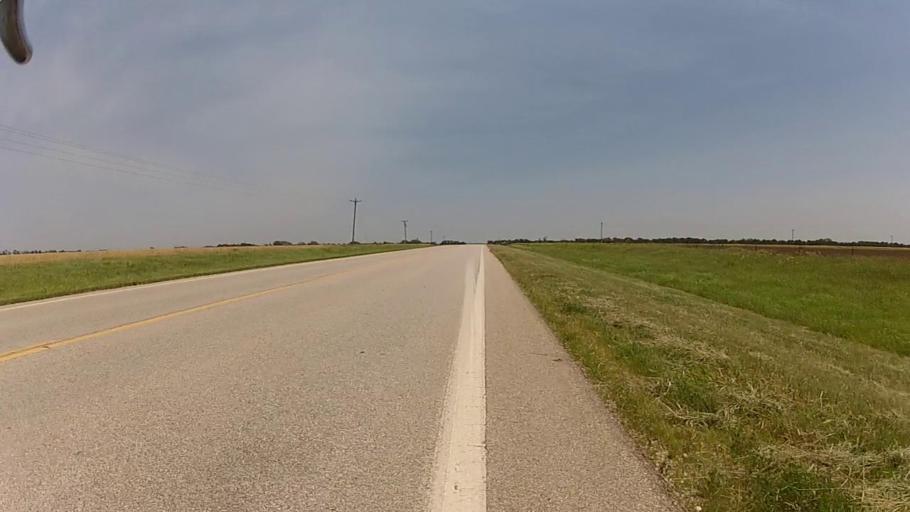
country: US
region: Kansas
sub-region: Cowley County
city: Arkansas City
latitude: 37.0569
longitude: -97.2218
